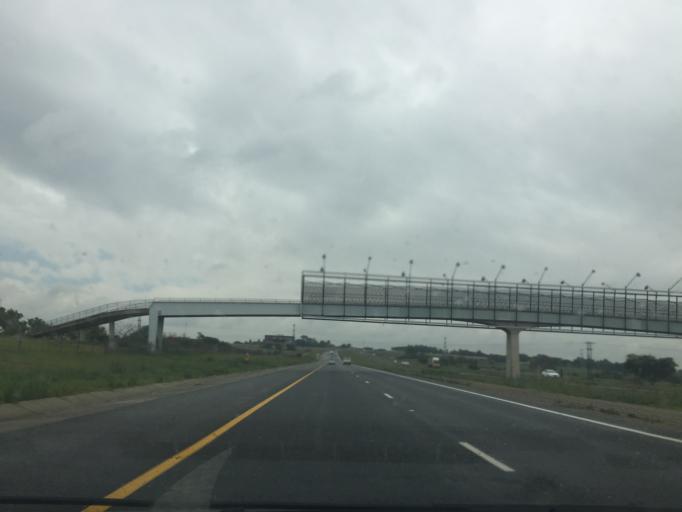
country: ZA
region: Gauteng
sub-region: City of Johannesburg Metropolitan Municipality
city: Diepsloot
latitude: -25.9593
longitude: 27.9516
